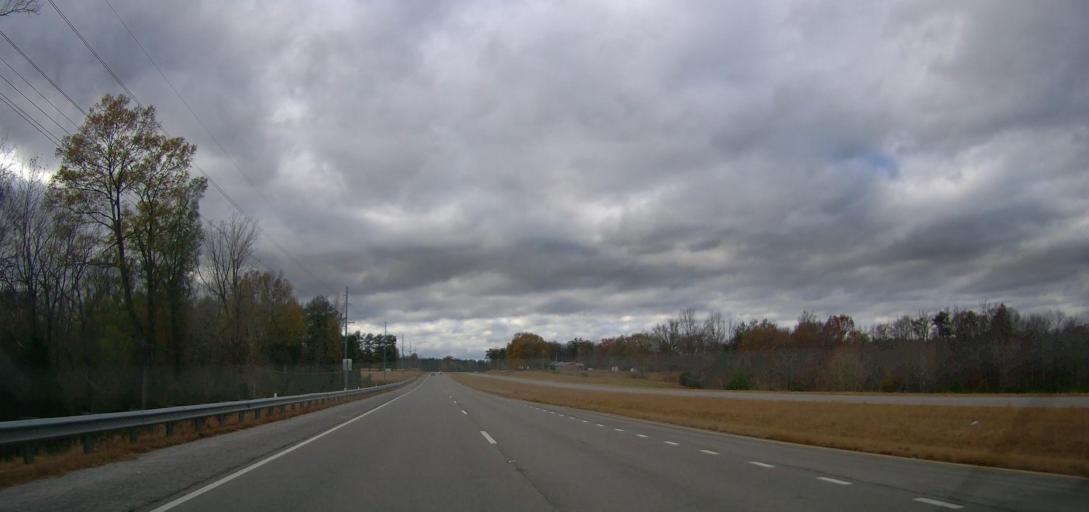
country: US
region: Alabama
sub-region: Lawrence County
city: Town Creek
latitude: 34.5721
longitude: -87.3911
